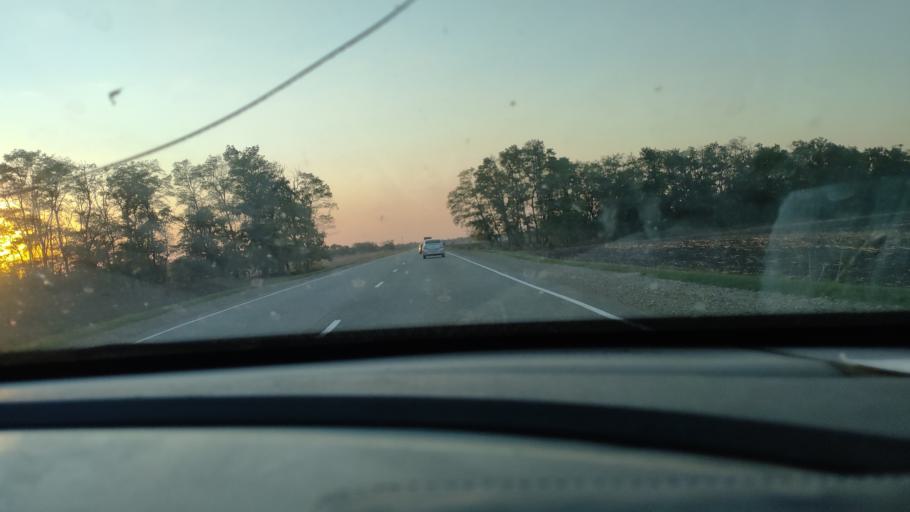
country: RU
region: Krasnodarskiy
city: Starominskaya
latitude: 46.4981
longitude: 39.0488
